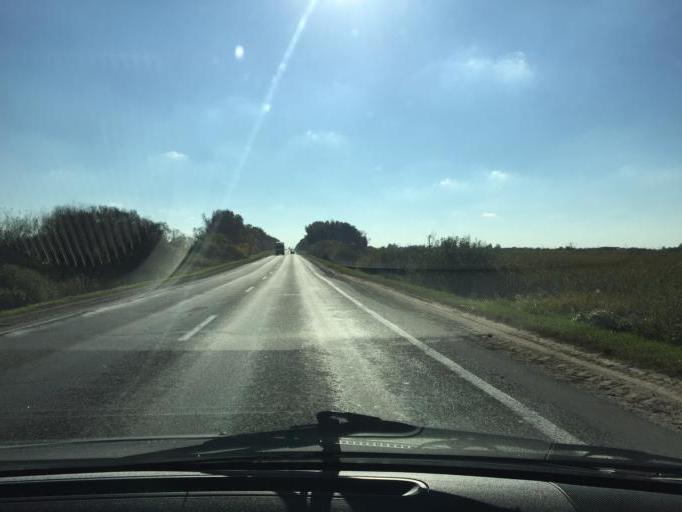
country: BY
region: Minsk
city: Slutsk
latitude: 52.9754
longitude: 27.5023
